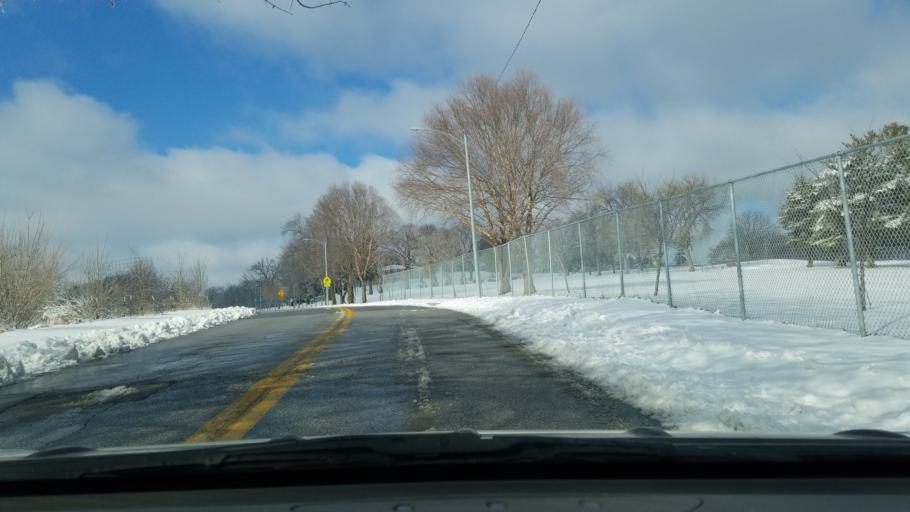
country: US
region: Nebraska
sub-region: Douglas County
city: Omaha
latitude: 41.2192
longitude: -95.9362
